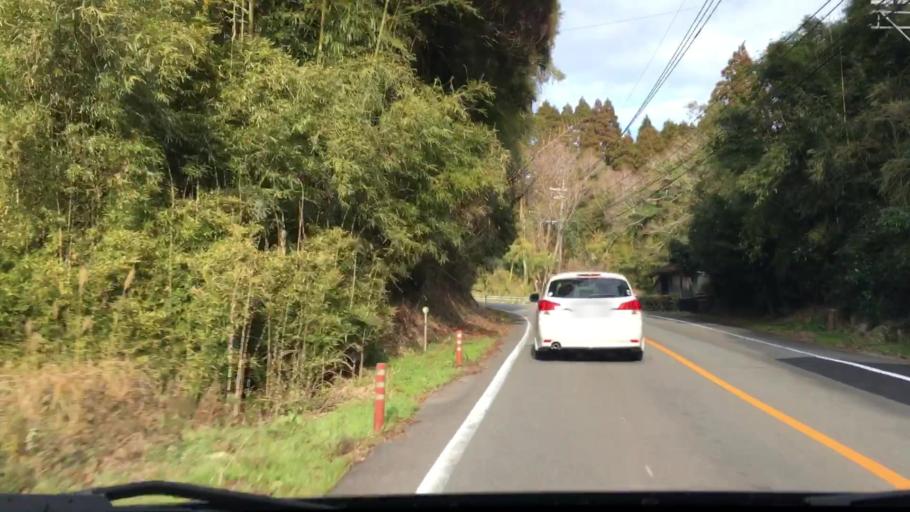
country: JP
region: Miyazaki
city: Nichinan
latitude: 31.7232
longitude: 131.3290
